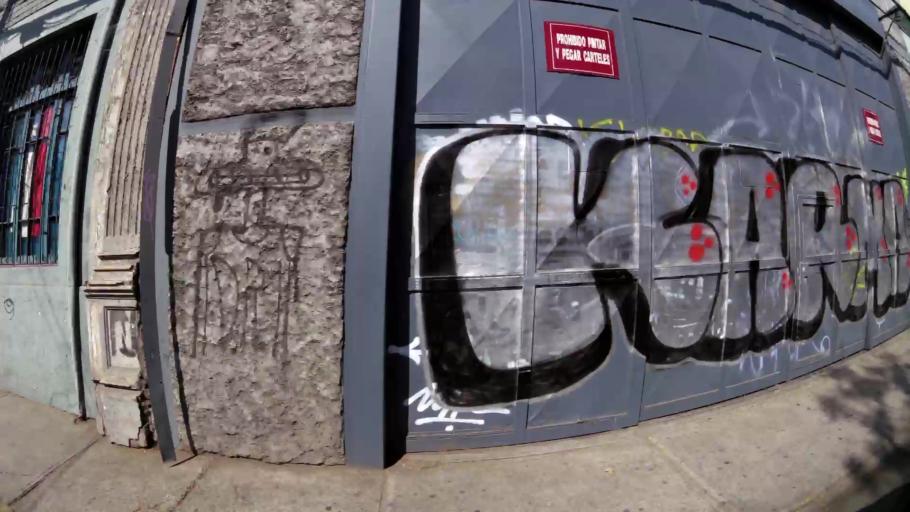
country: CL
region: Santiago Metropolitan
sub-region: Provincia de Santiago
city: Santiago
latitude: -33.4310
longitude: -70.6381
